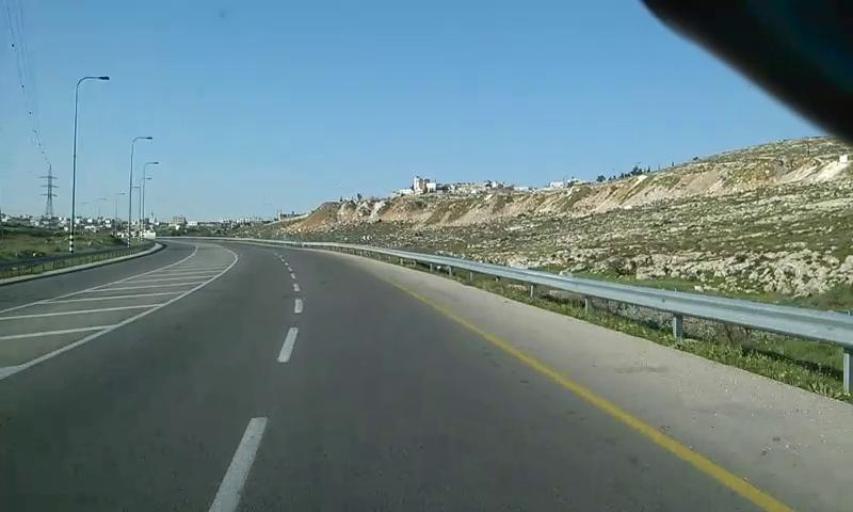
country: PS
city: Bayt `Inun
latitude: 31.5557
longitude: 35.1354
